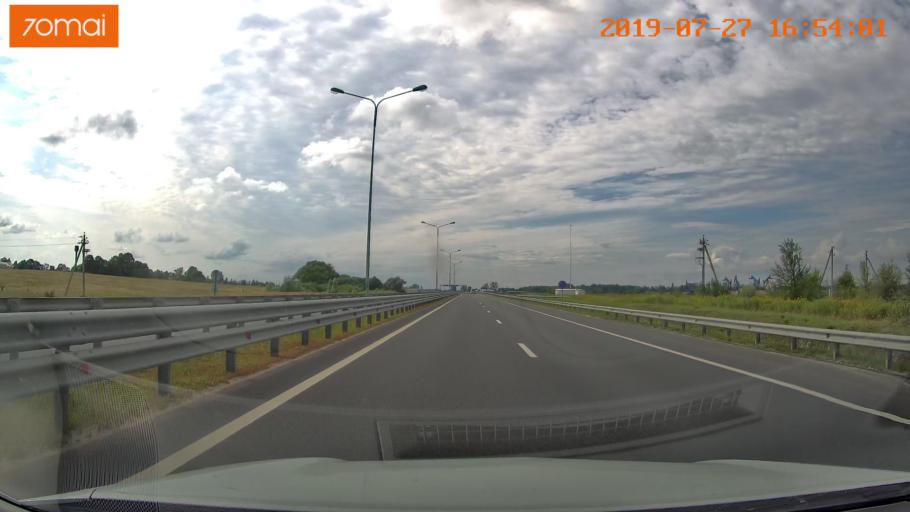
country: RU
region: Kaliningrad
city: Bol'shoe Isakovo
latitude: 54.6921
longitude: 20.8179
